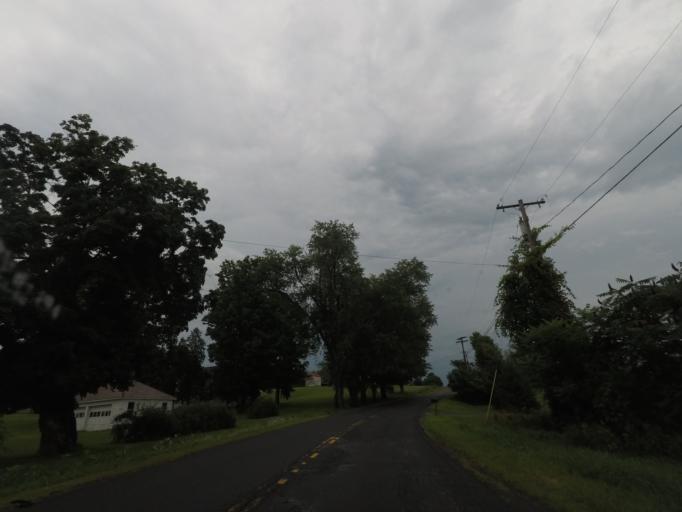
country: US
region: New York
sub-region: Rensselaer County
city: Poestenkill
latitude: 42.8043
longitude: -73.5635
